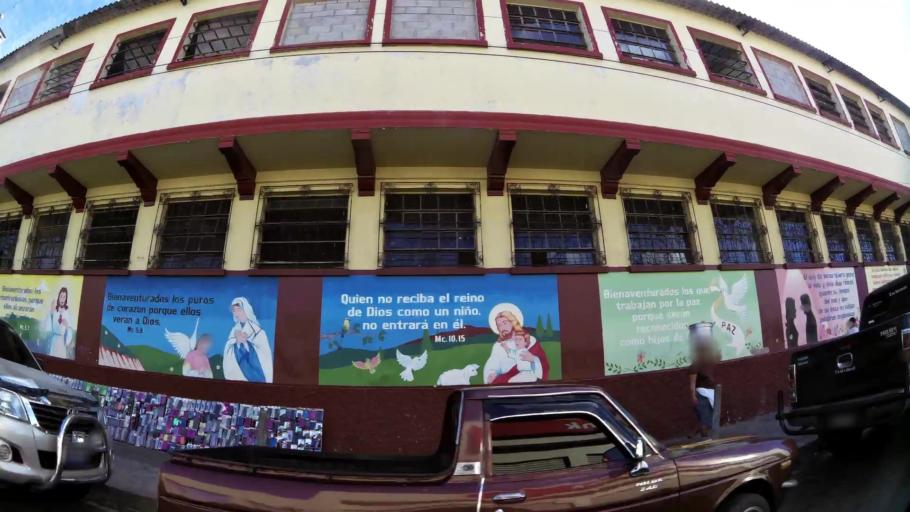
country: SV
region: Cuscatlan
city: Cojutepeque
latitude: 13.7224
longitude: -88.9356
